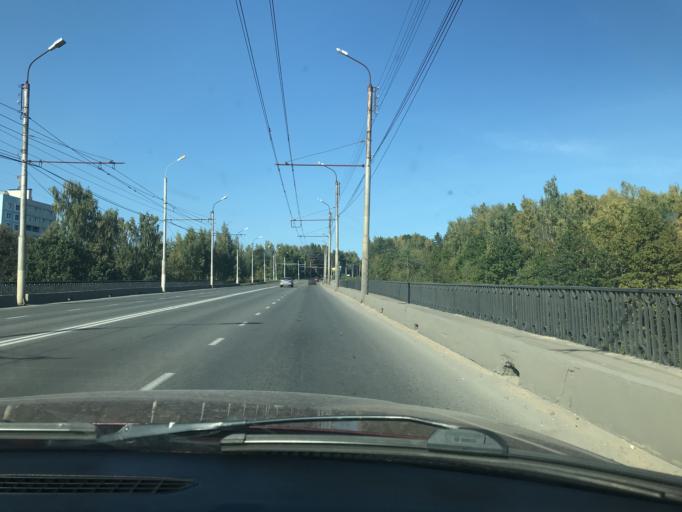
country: RU
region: Kaluga
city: Kaluga
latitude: 54.5674
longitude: 36.2579
